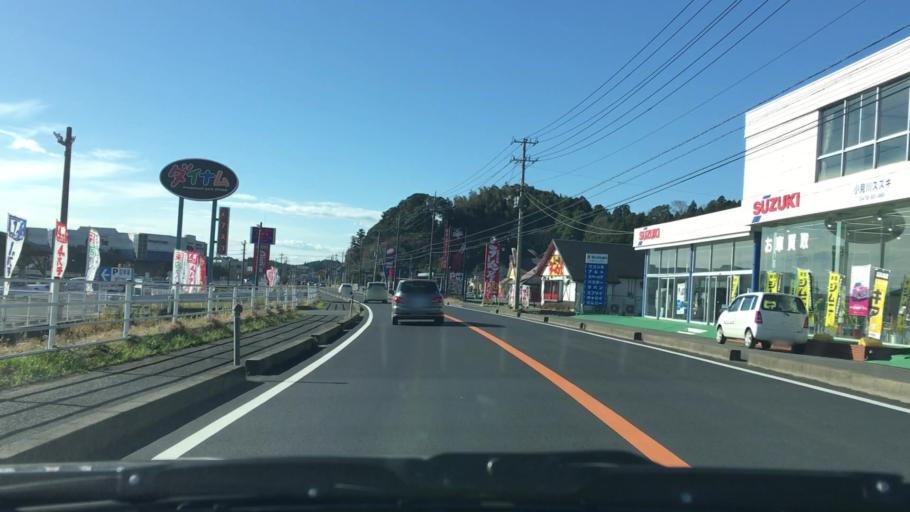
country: JP
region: Chiba
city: Omigawa
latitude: 35.8524
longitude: 140.5826
